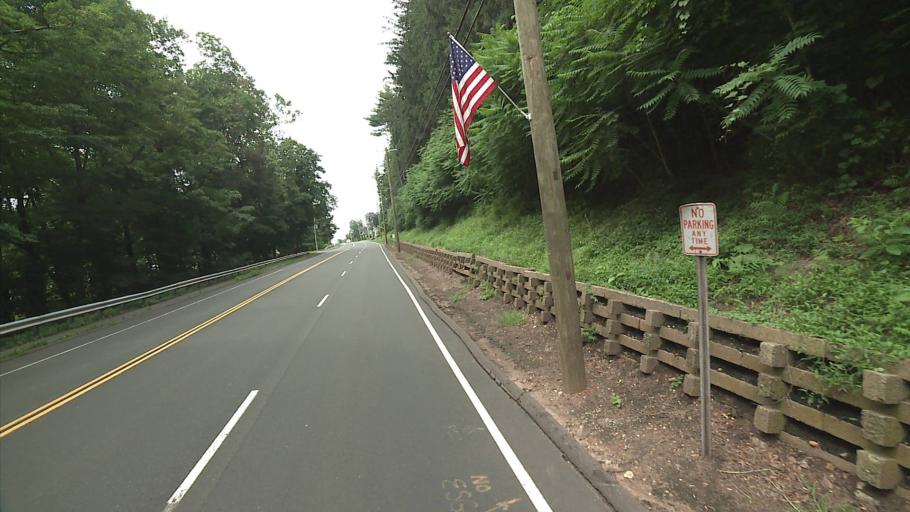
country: US
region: Connecticut
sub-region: Middlesex County
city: Cromwell
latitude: 41.6073
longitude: -72.6494
